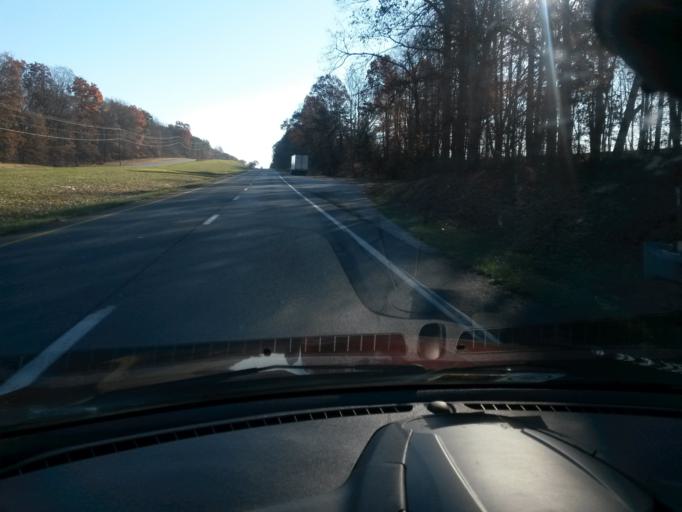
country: US
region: Virginia
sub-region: Appomattox County
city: Appomattox
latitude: 37.2859
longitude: -78.7213
